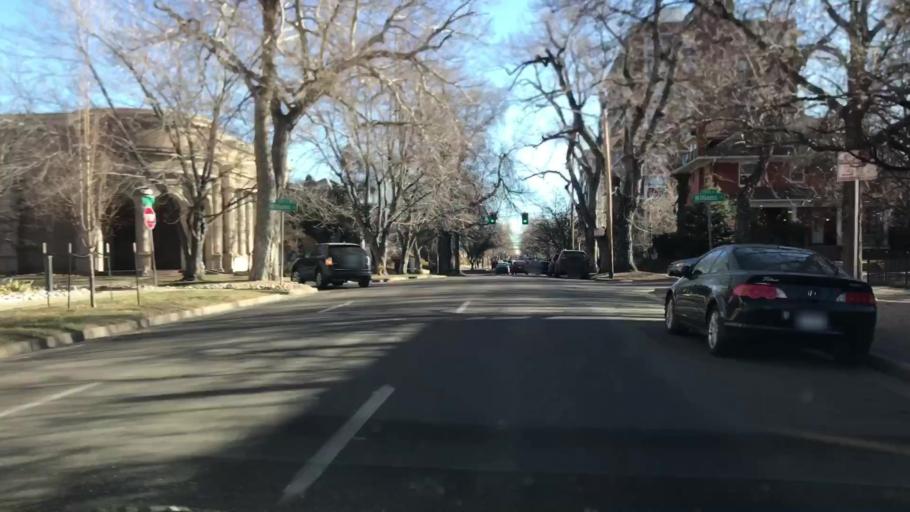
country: US
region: Colorado
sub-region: Denver County
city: Denver
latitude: 39.7384
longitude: -104.9664
